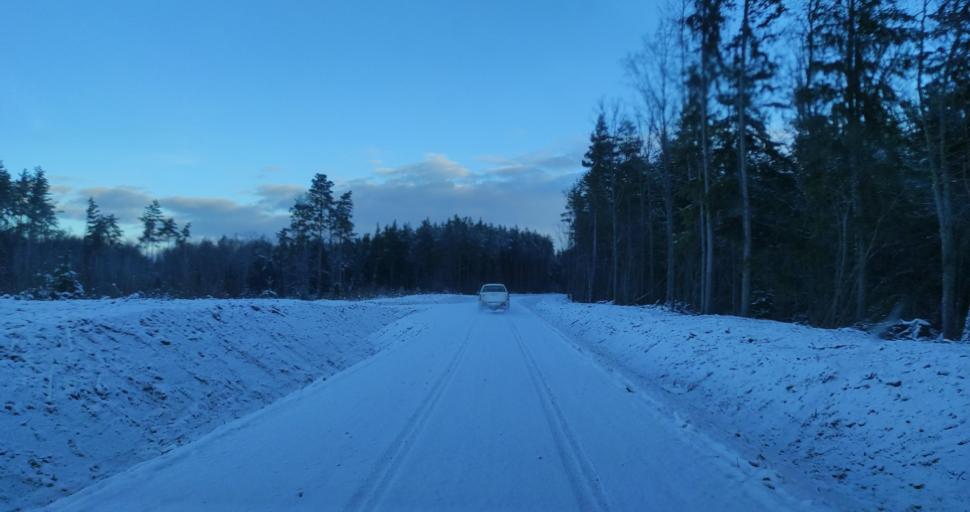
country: LV
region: Skrunda
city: Skrunda
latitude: 56.5868
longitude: 21.9518
